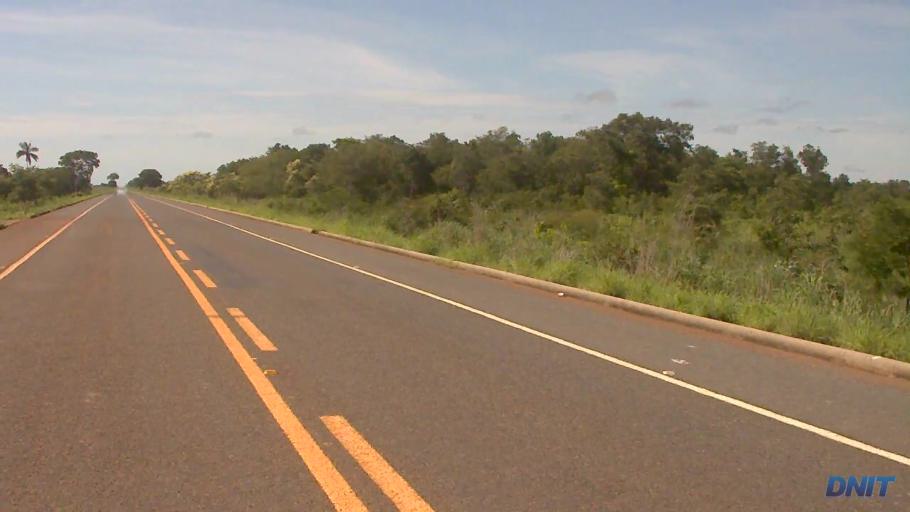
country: BR
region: Goias
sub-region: Sao Miguel Do Araguaia
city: Sao Miguel do Araguaia
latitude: -13.4107
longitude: -50.1322
